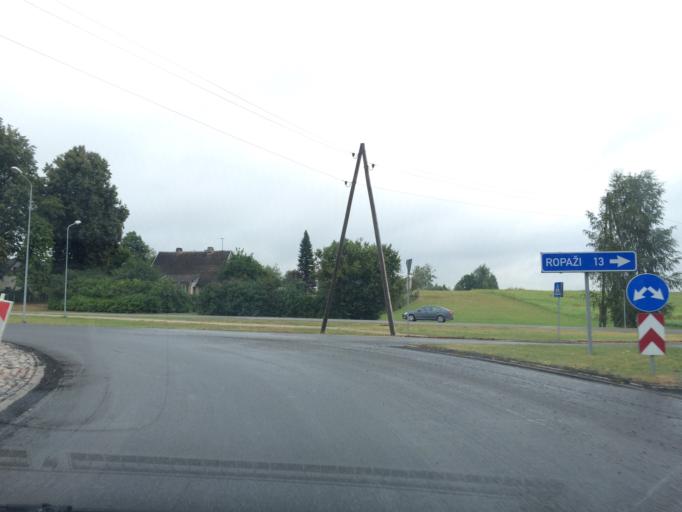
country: LV
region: Ikskile
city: Ikskile
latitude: 56.8644
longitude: 24.5610
